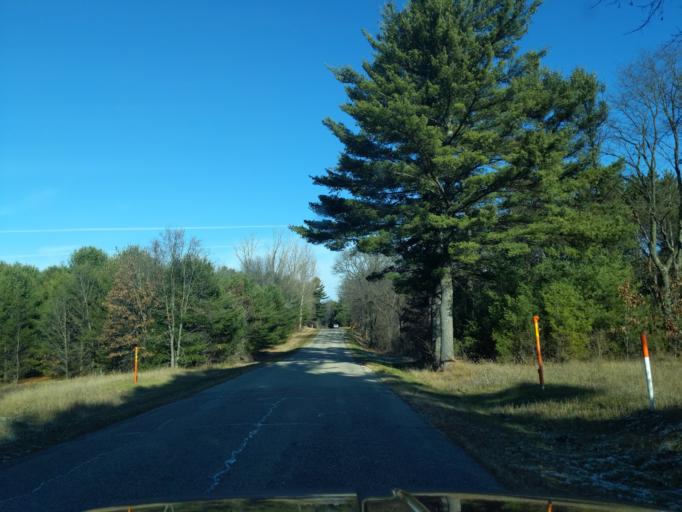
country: US
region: Wisconsin
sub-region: Waushara County
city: Silver Lake
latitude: 44.0813
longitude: -89.1938
